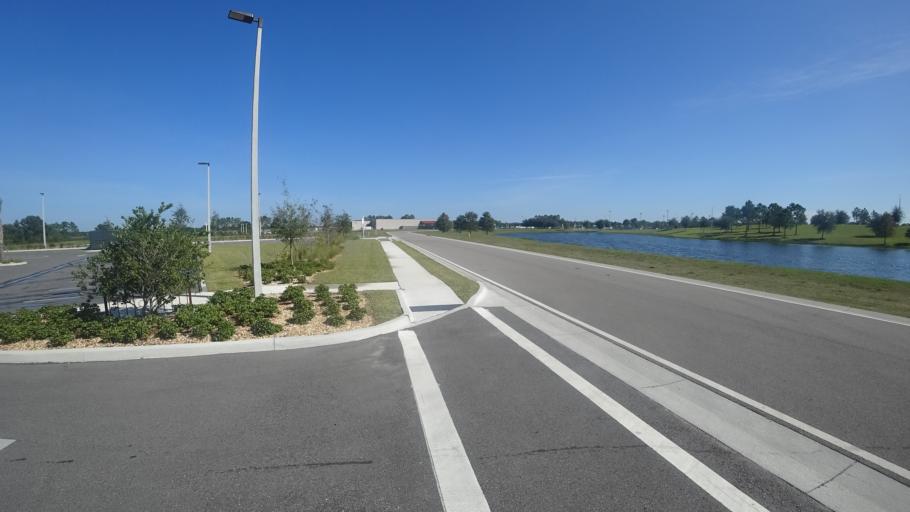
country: US
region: Florida
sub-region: Sarasota County
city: The Meadows
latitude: 27.4326
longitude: -82.3864
